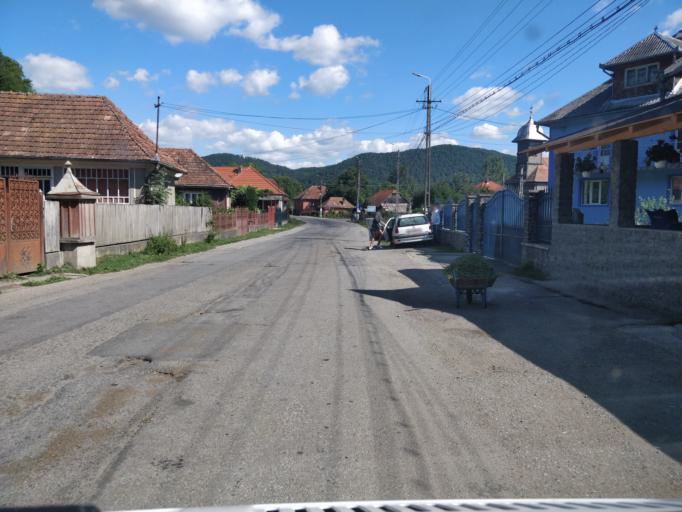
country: RO
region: Cluj
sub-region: Comuna Poeni
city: Poeni
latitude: 46.8789
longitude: 22.8795
